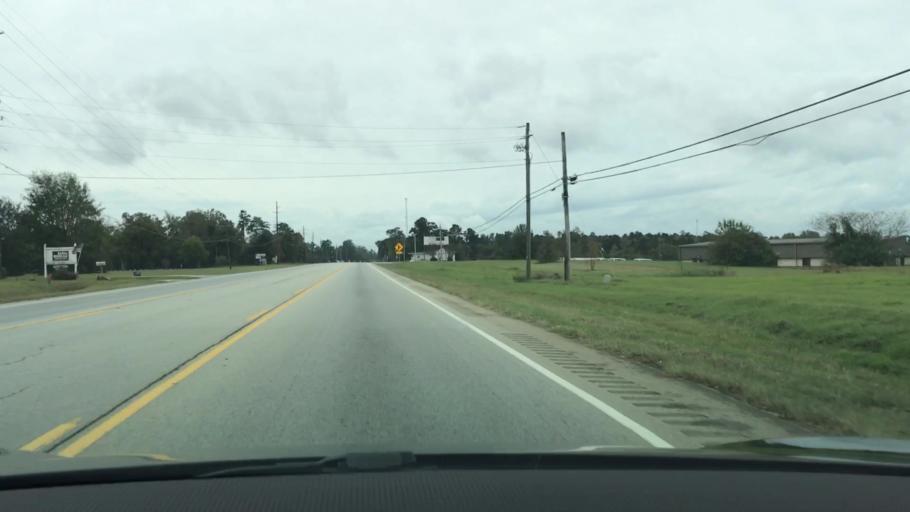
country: US
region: Georgia
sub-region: Jefferson County
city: Louisville
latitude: 33.0227
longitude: -82.4045
